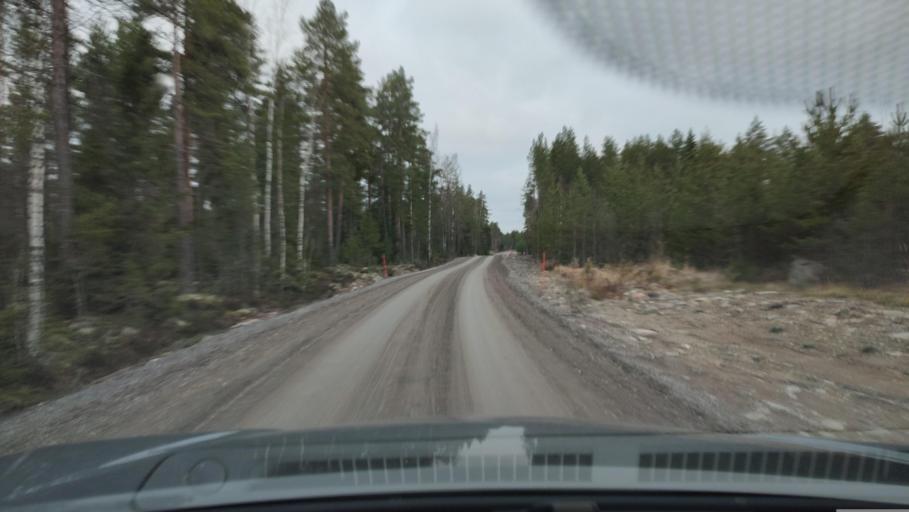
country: FI
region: Southern Ostrobothnia
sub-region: Suupohja
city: Karijoki
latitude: 62.1920
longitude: 21.5883
